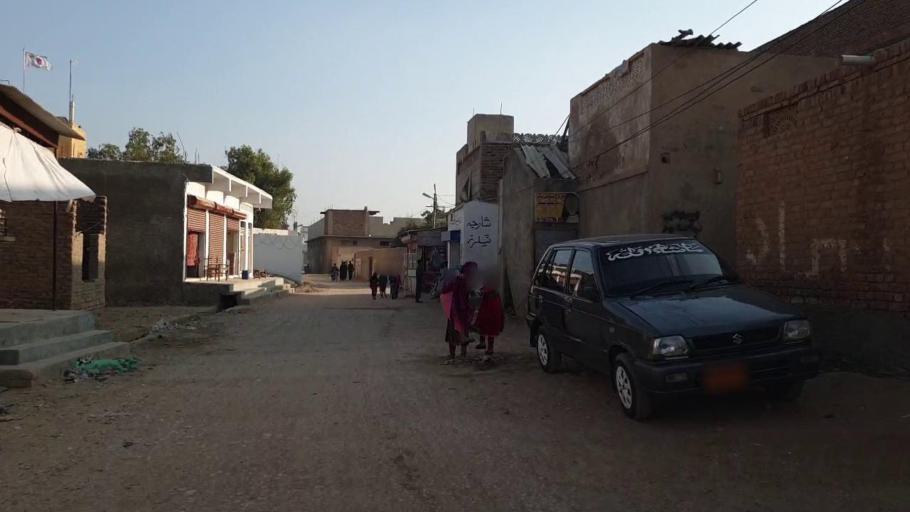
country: PK
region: Sindh
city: Kotri
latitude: 25.3552
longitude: 68.2642
